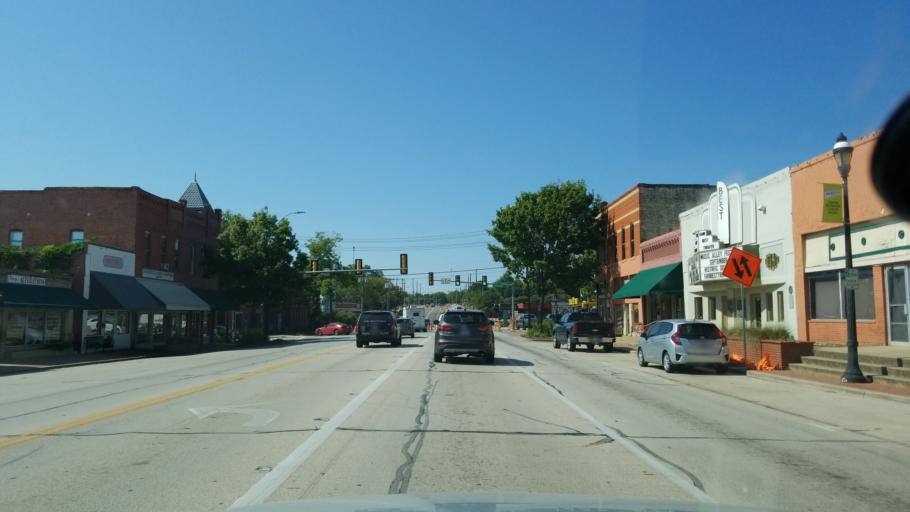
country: US
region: Texas
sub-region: Tarrant County
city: Mansfield
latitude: 32.5642
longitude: -97.1419
